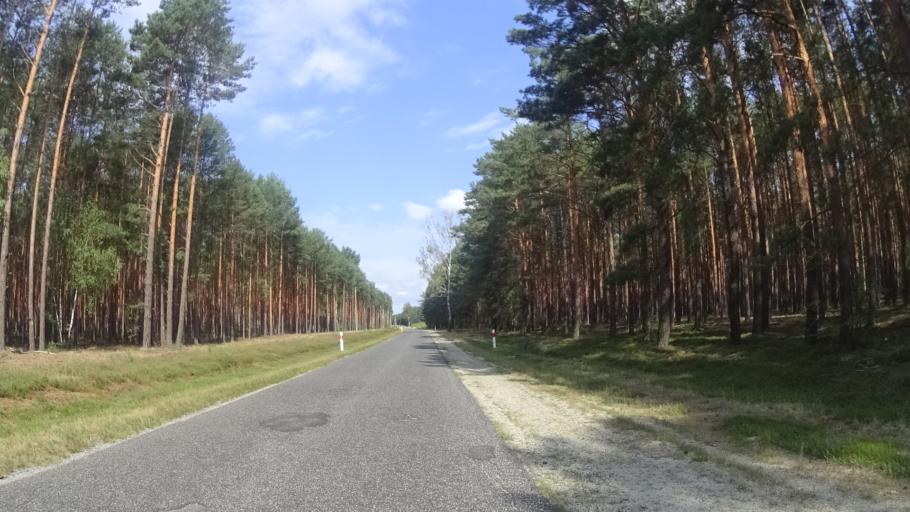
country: PL
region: Lubusz
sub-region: Powiat zarski
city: Leknica
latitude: 51.5143
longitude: 14.8324
